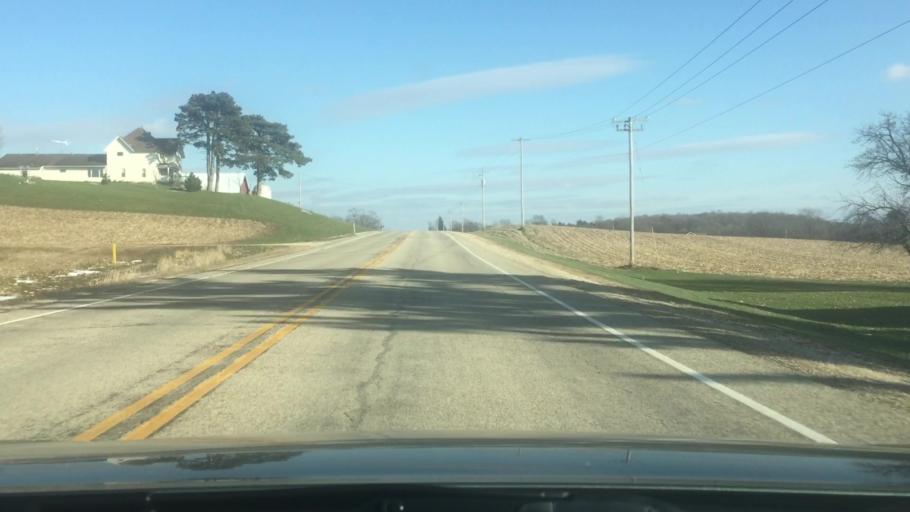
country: US
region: Wisconsin
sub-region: Jefferson County
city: Palmyra
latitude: 42.9326
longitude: -88.6653
